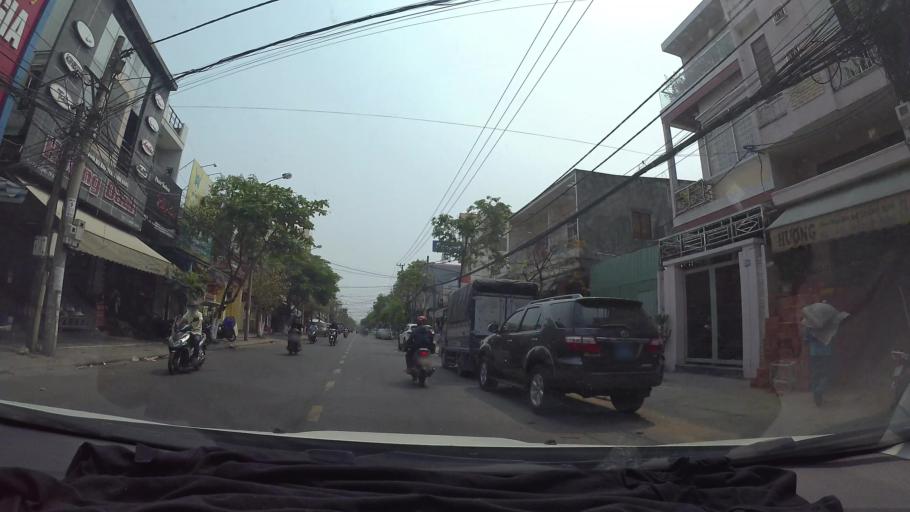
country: VN
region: Da Nang
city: Son Tra
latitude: 16.0441
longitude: 108.2214
